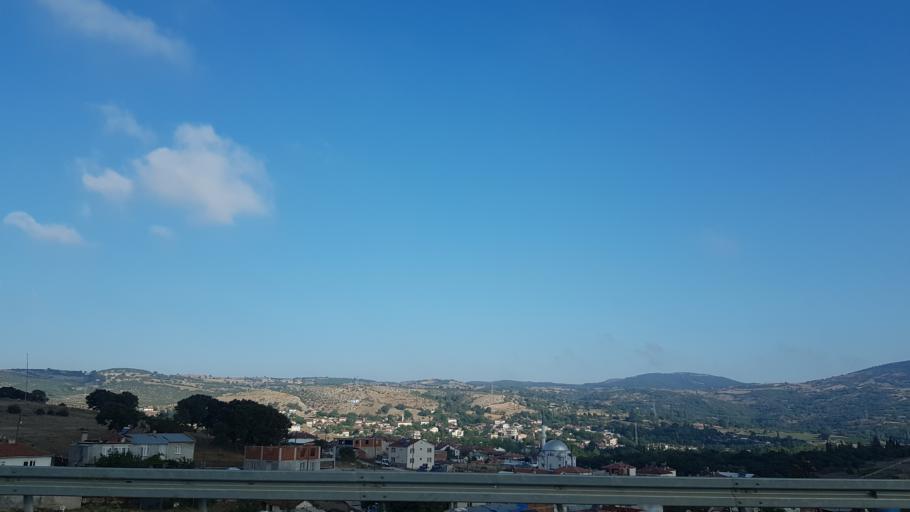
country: TR
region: Balikesir
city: Yenikoy
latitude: 39.7720
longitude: 28.0116
